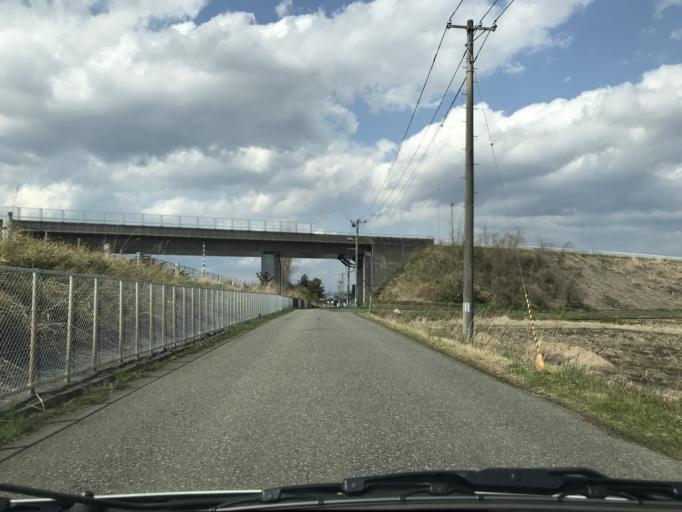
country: JP
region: Iwate
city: Mizusawa
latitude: 39.1338
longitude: 141.1198
